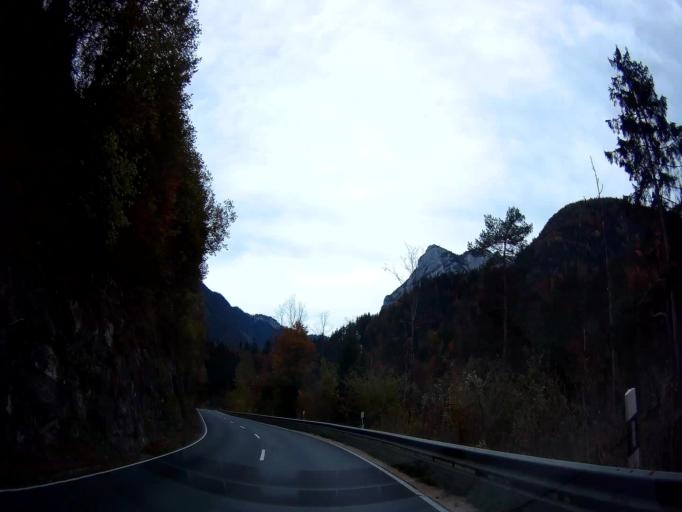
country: DE
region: Bavaria
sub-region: Upper Bavaria
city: Schneizlreuth
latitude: 47.6884
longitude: 12.8050
